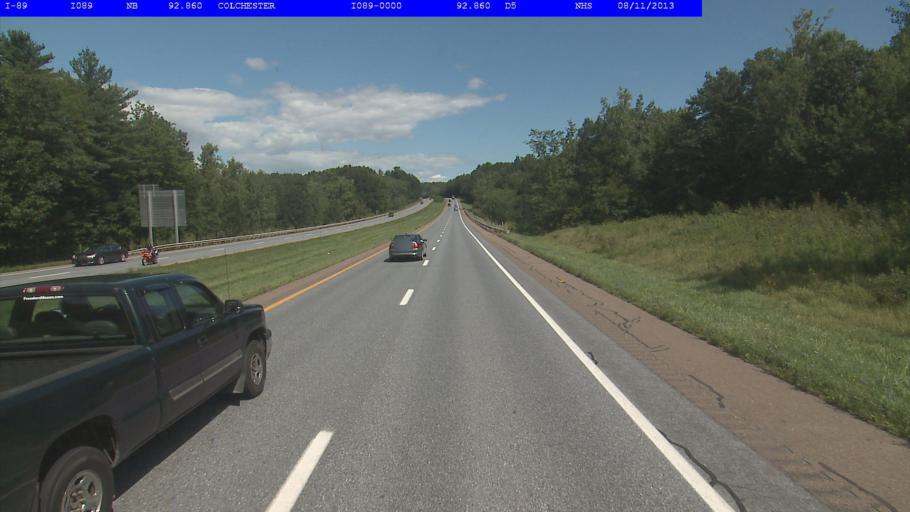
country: US
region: Vermont
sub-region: Chittenden County
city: Winooski
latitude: 44.5219
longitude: -73.1927
